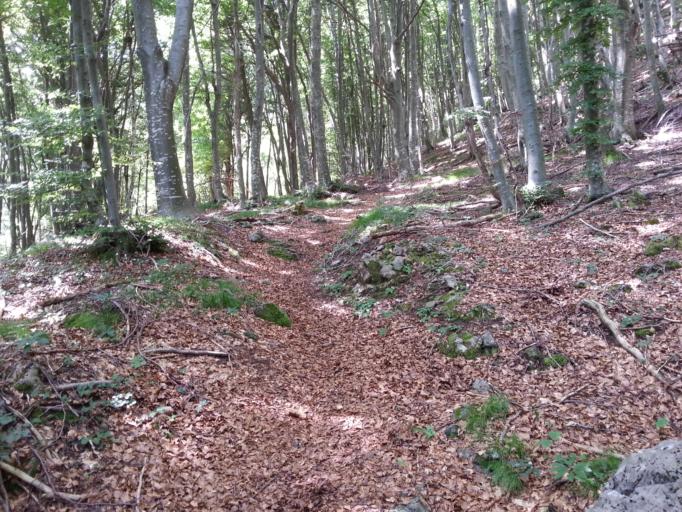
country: IT
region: Lombardy
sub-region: Provincia di Lecco
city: Cremeno
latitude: 45.9106
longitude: 9.4542
